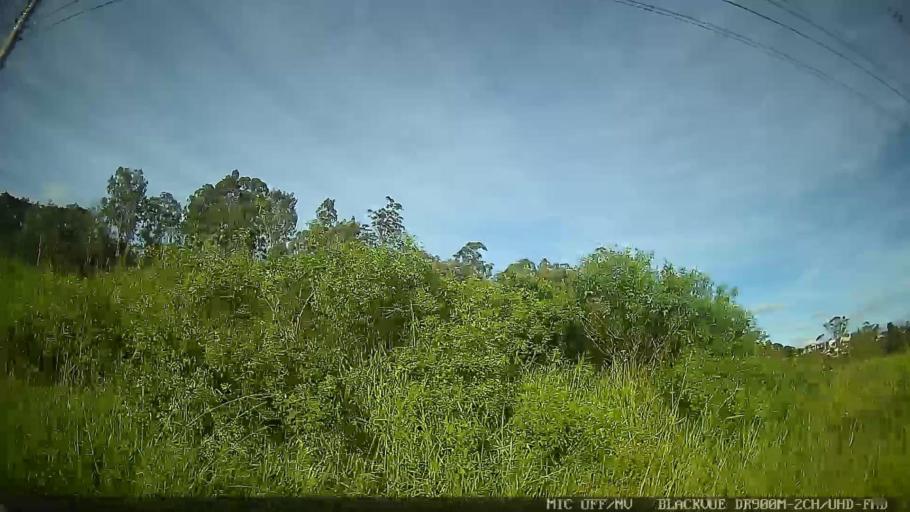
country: BR
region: Sao Paulo
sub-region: Mogi das Cruzes
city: Mogi das Cruzes
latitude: -23.5195
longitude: -46.1490
